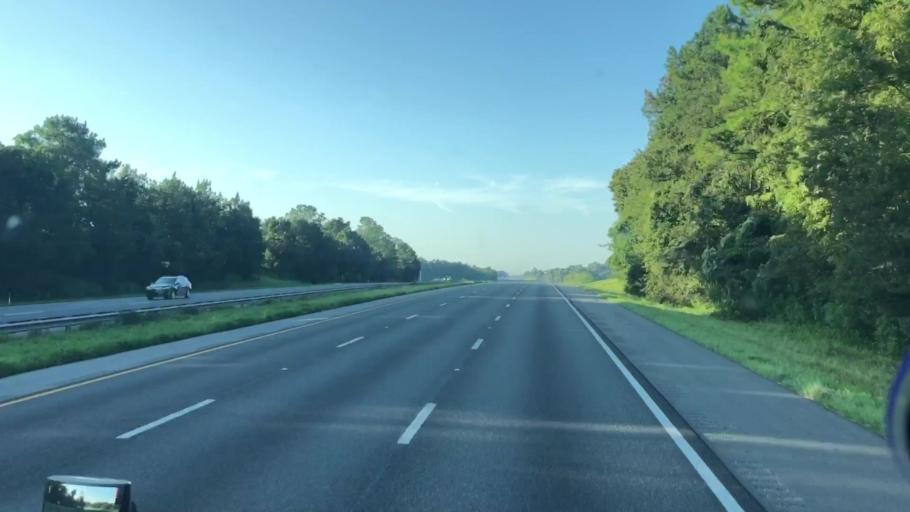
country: US
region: Florida
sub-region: Marion County
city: Citra
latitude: 29.3327
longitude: -82.2150
